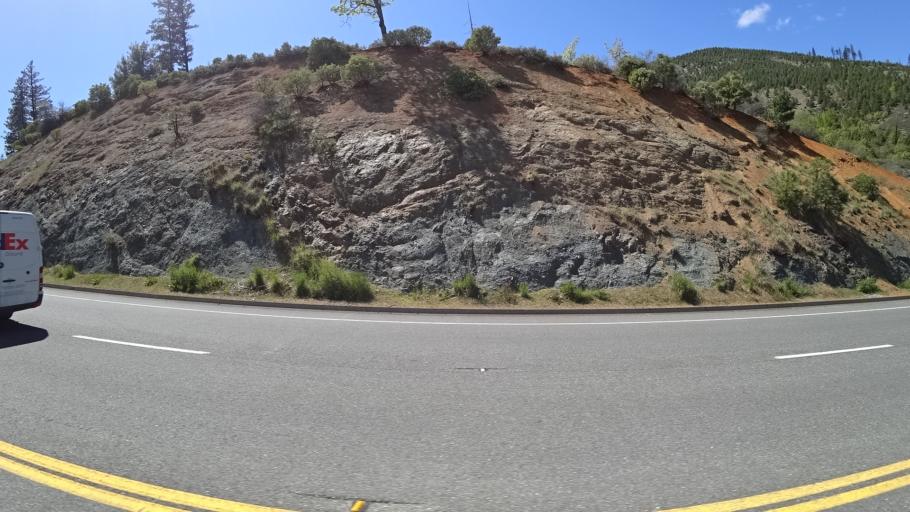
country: US
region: California
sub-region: Trinity County
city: Weaverville
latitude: 40.7427
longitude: -122.9765
